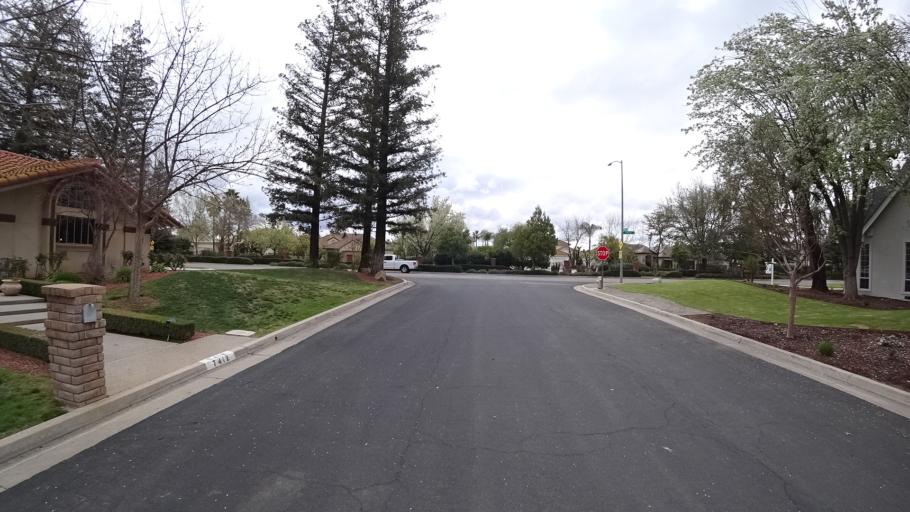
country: US
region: California
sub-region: Fresno County
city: Fresno
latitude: 36.8447
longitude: -119.8390
